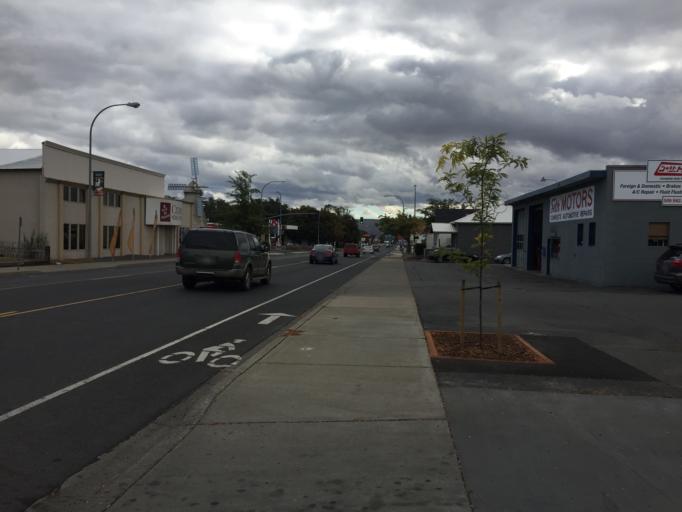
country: US
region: Washington
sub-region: Kittitas County
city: Ellensburg
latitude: 46.9922
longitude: -120.5486
